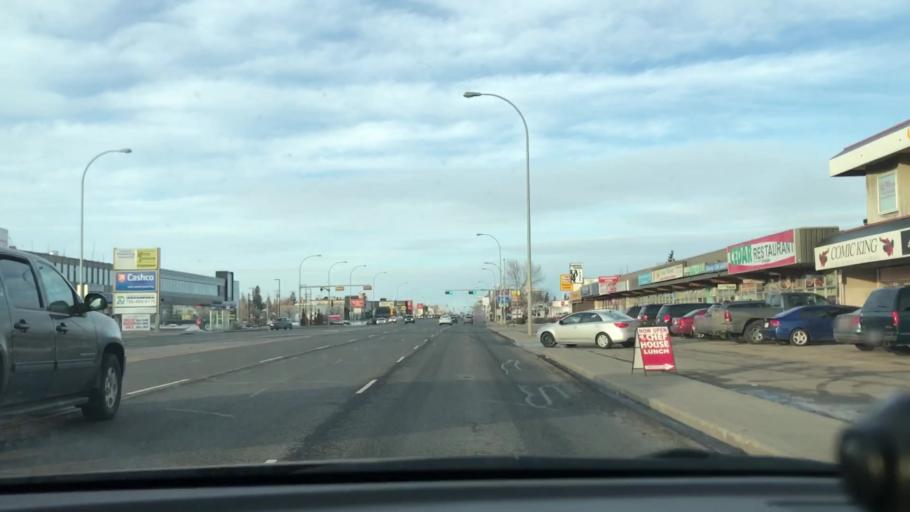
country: CA
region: Alberta
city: Edmonton
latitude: 53.5878
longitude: -113.4919
